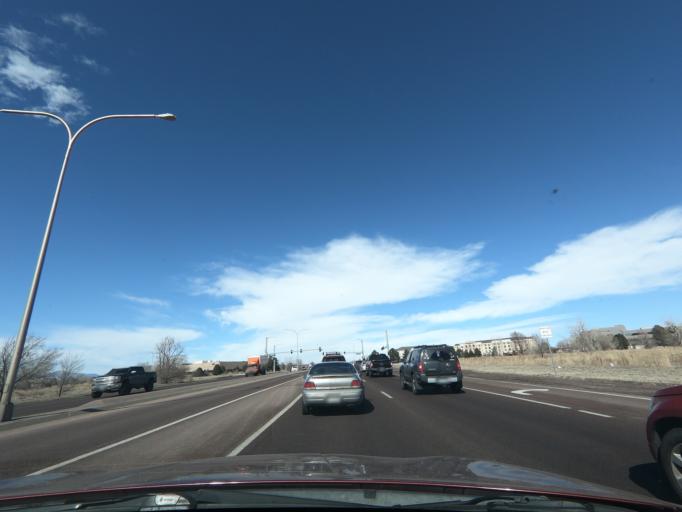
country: US
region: Colorado
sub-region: El Paso County
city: Stratmoor
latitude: 38.8049
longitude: -104.7302
